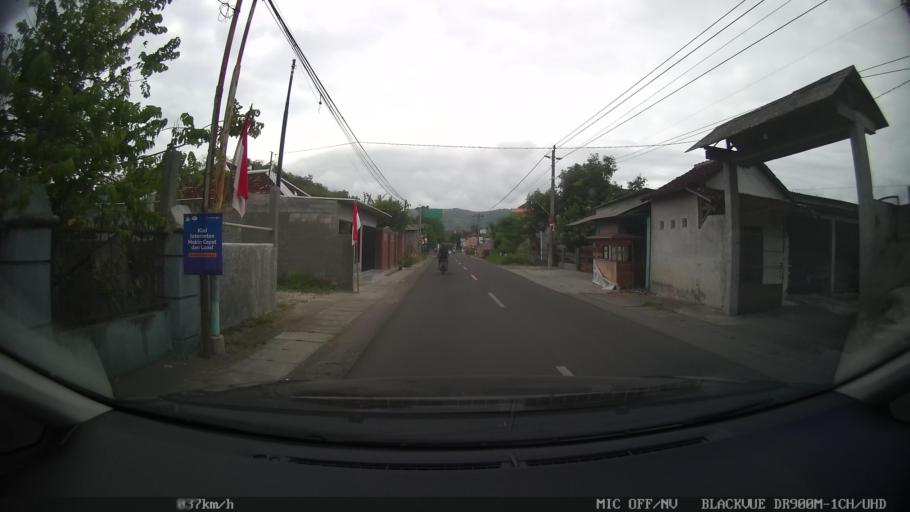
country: ID
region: Daerah Istimewa Yogyakarta
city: Sewon
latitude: -7.8796
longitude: 110.4172
